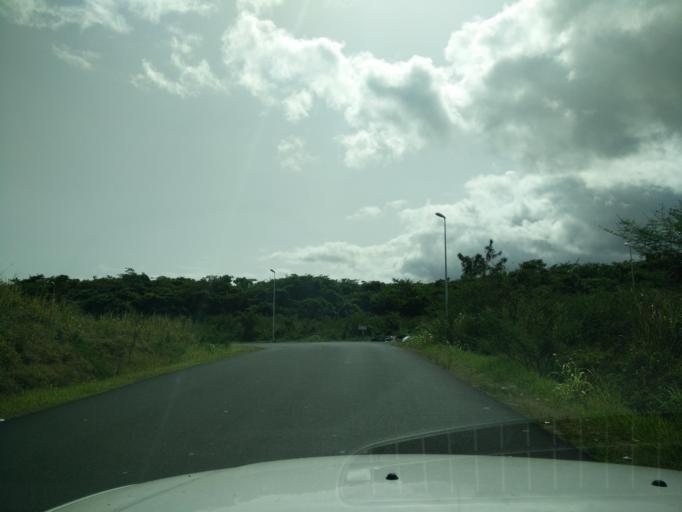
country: GP
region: Guadeloupe
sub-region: Guadeloupe
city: Baie-Mahault
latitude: 16.2477
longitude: -61.5718
